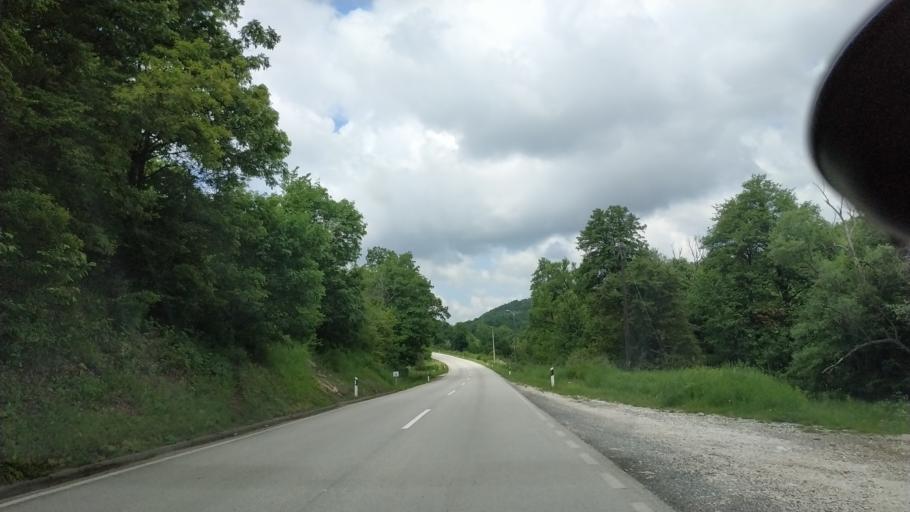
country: RS
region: Central Serbia
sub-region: Borski Okrug
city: Bor
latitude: 44.0684
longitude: 22.0346
